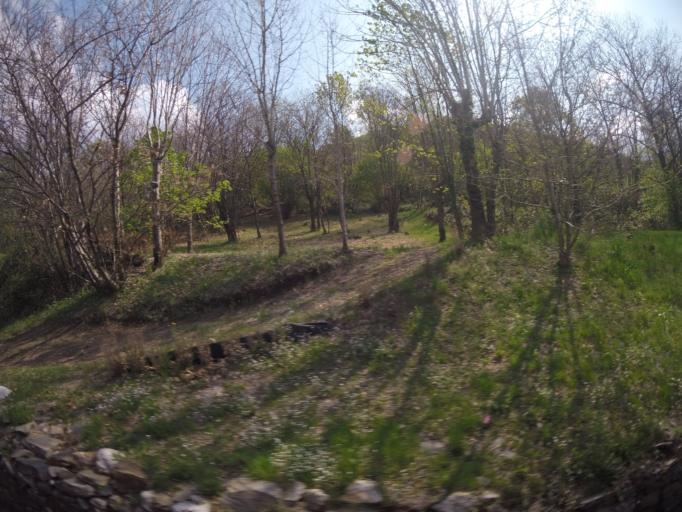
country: IT
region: Piedmont
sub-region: Provincia di Novara
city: Pettenasco
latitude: 45.8375
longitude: 8.3999
